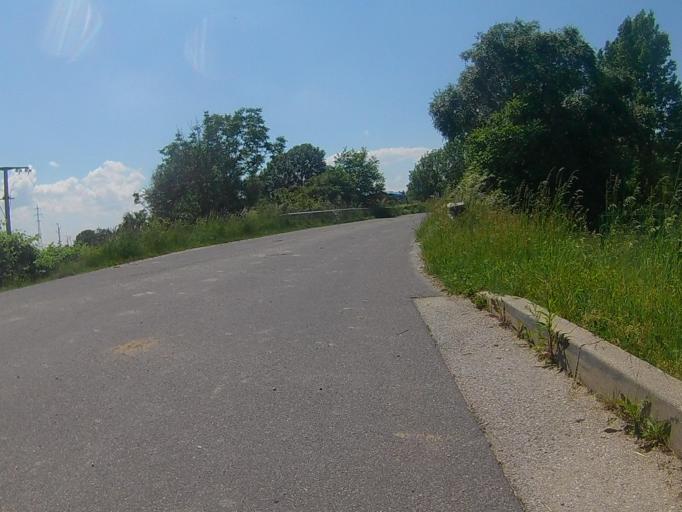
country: SI
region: Hoce-Slivnica
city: Radizel
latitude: 46.4774
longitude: 15.6602
